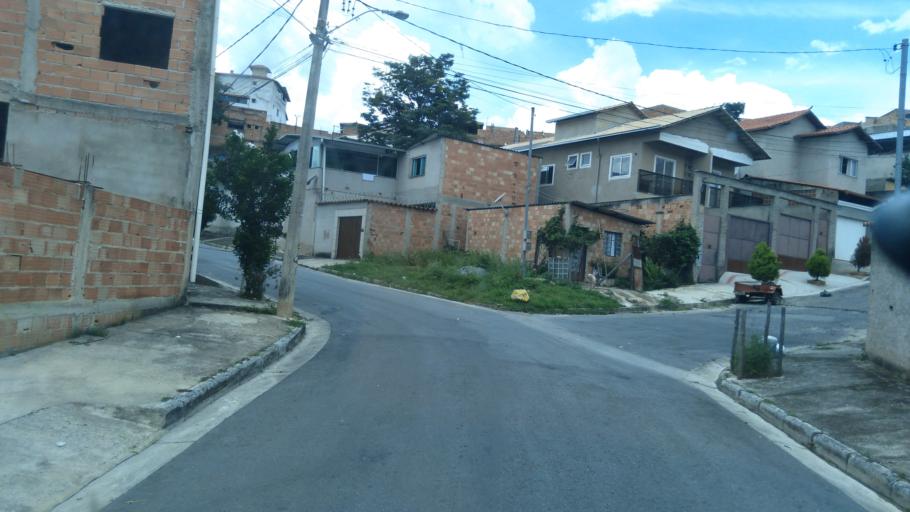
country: BR
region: Minas Gerais
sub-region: Belo Horizonte
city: Belo Horizonte
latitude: -19.8584
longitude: -43.8762
